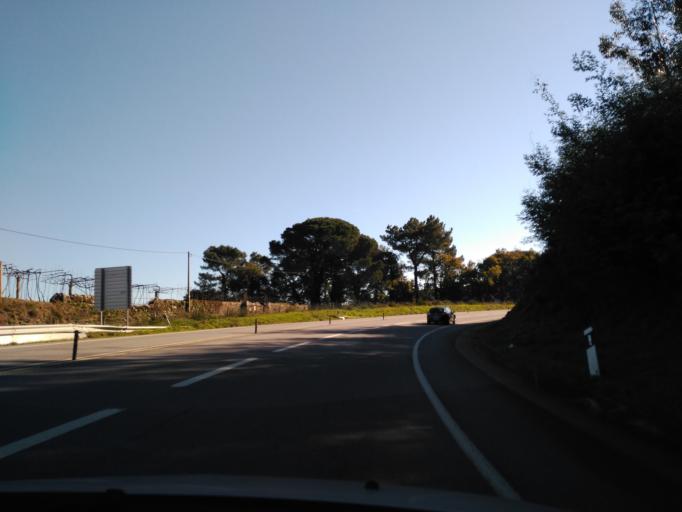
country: PT
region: Braga
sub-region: Amares
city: Amares
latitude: 41.5927
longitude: -8.3430
